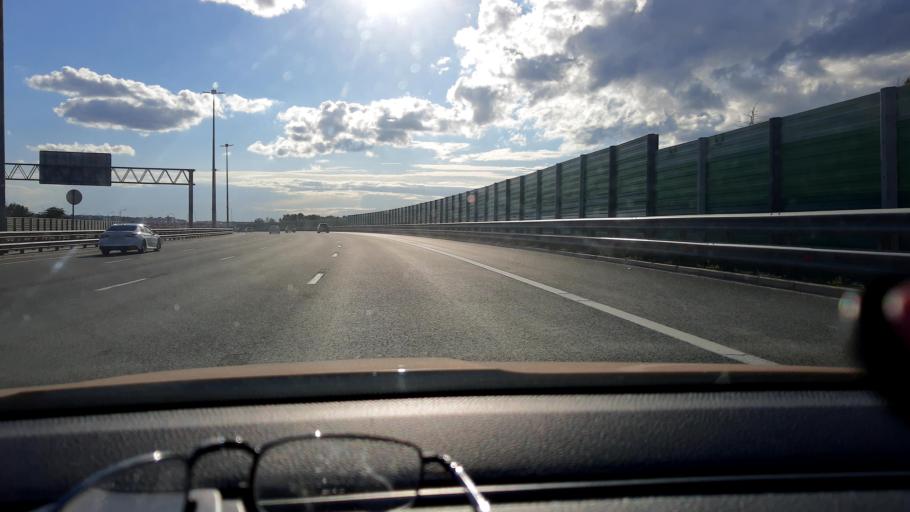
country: RU
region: Moskovskaya
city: Nemchinovka
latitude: 55.7307
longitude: 37.3576
